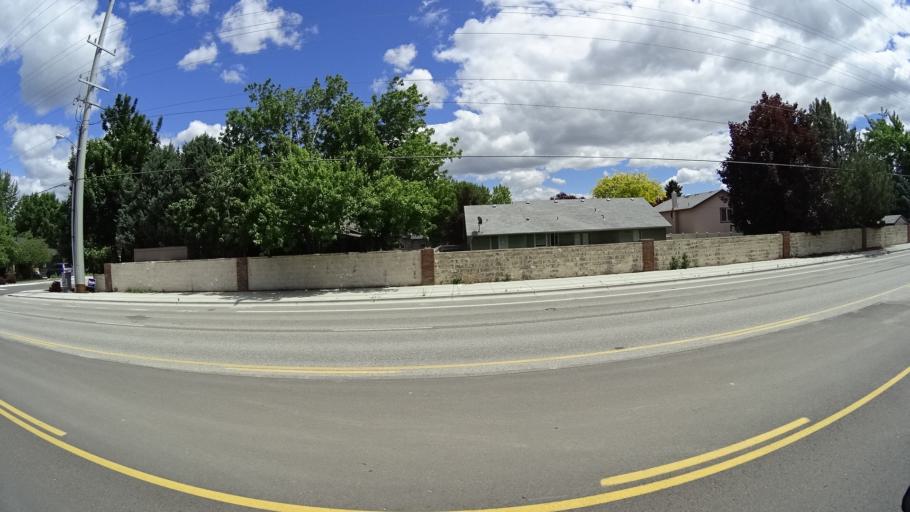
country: US
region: Idaho
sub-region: Ada County
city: Eagle
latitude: 43.6367
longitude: -116.3345
